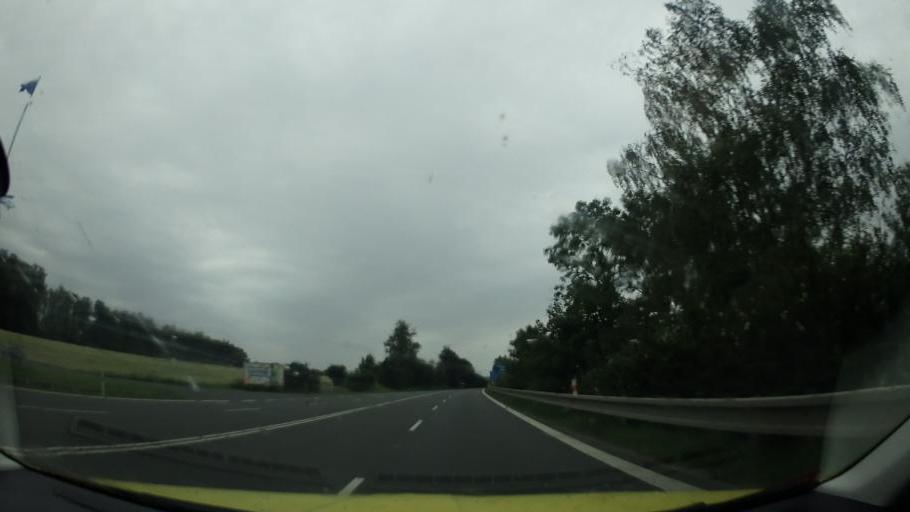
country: CZ
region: Olomoucky
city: Belotin
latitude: 49.5759
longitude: 17.7782
